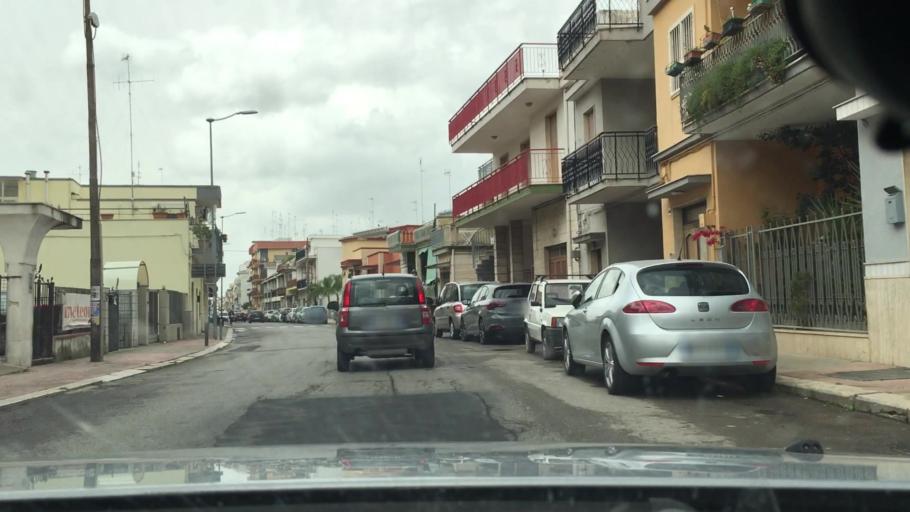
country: IT
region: Apulia
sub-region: Provincia di Bari
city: Capurso
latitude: 41.0472
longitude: 16.9272
